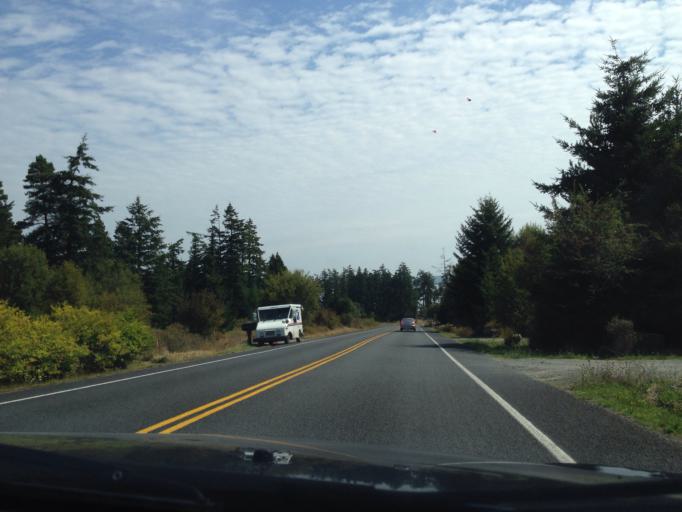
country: US
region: Washington
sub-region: San Juan County
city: Friday Harbor
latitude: 48.5108
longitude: -123.0277
